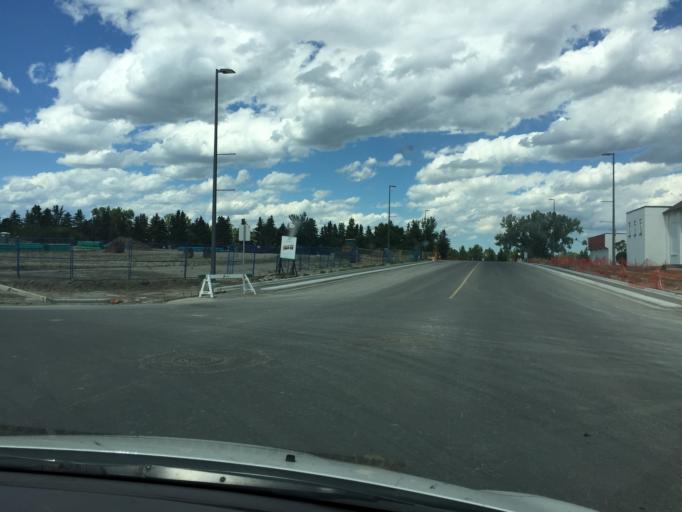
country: CA
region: Alberta
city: Calgary
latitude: 51.0178
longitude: -114.1236
